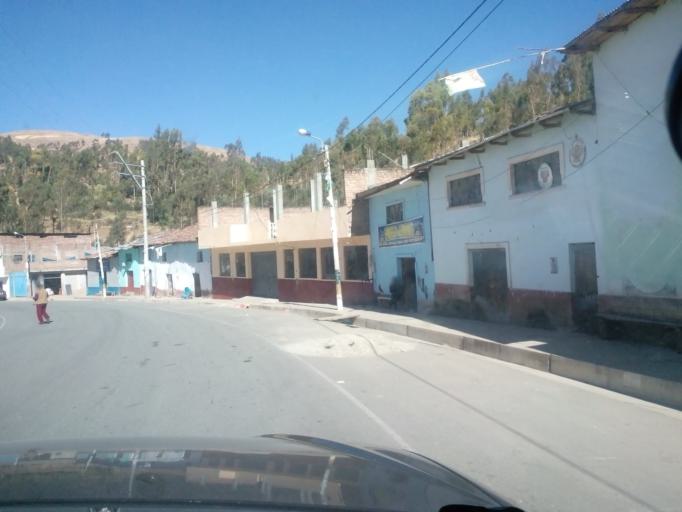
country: PE
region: Apurimac
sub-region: Provincia de Andahuaylas
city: Talavera
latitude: -13.6575
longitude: -73.4956
